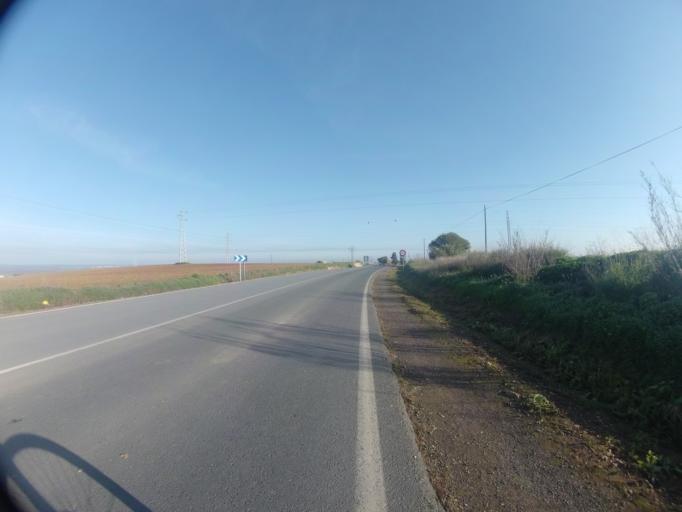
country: ES
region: Andalusia
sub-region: Provincia de Huelva
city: Huelva
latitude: 37.2933
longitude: -6.9311
